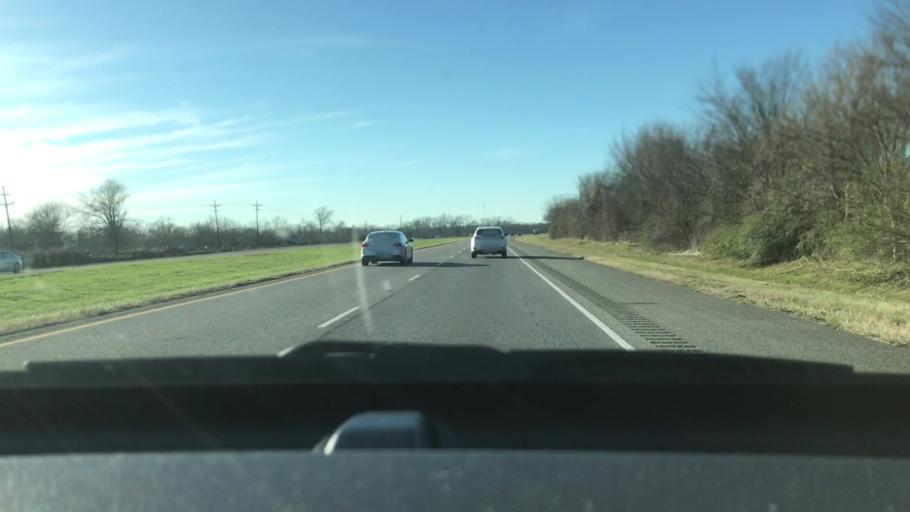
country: US
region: Louisiana
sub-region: Rapides Parish
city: Boyce
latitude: 31.3714
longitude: -92.6245
